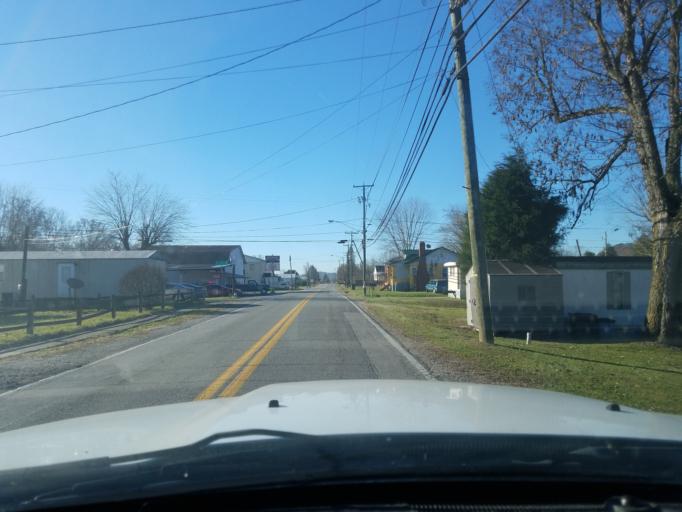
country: US
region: West Virginia
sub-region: Putnam County
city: Buffalo
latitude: 38.6155
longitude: -81.9835
